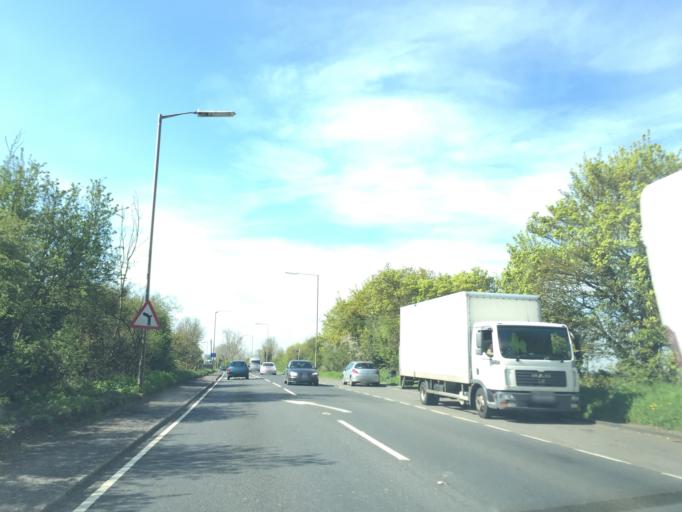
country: GB
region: England
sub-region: Essex
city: Epping
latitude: 51.7331
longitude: 0.1251
